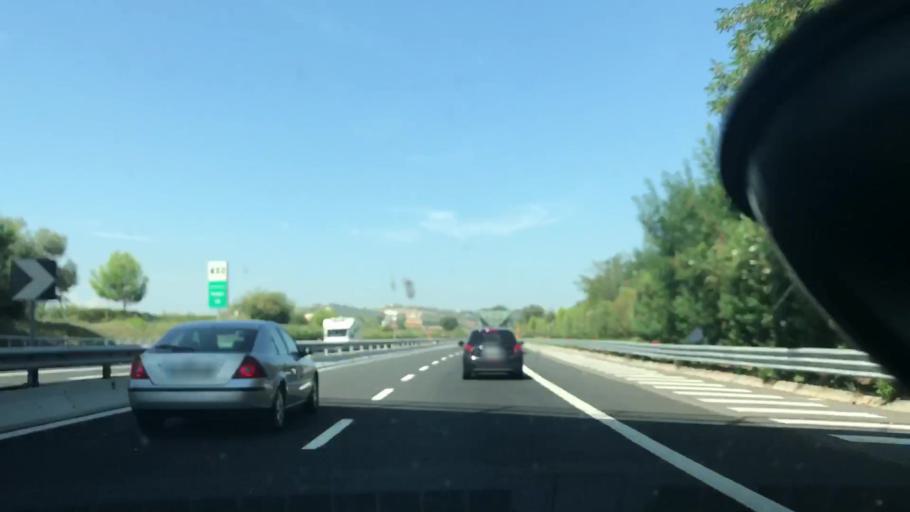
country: IT
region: Abruzzo
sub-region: Provincia di Chieti
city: San Salvo
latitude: 42.0551
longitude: 14.7495
